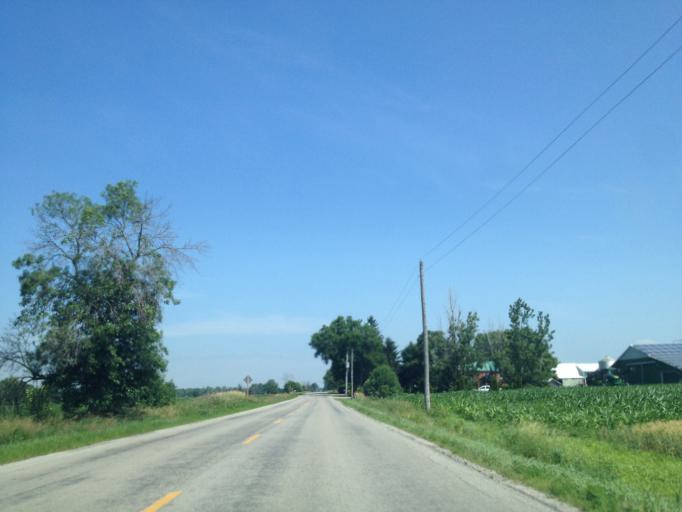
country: CA
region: Ontario
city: London
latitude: 43.1309
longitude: -81.2078
